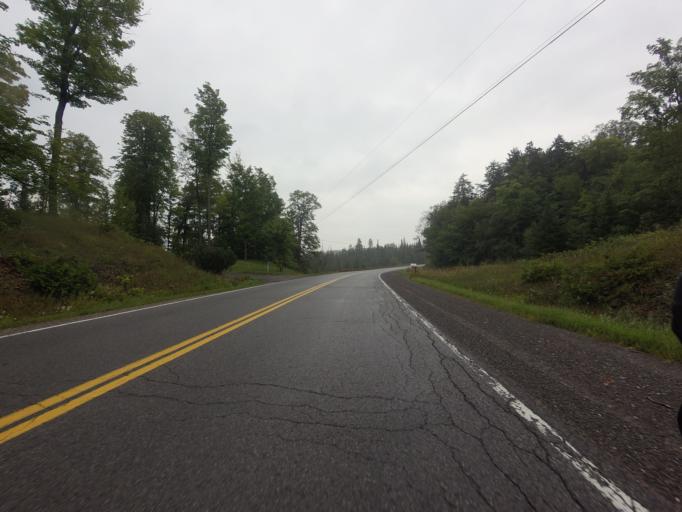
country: CA
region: Ontario
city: Carleton Place
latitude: 45.1114
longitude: -76.3688
